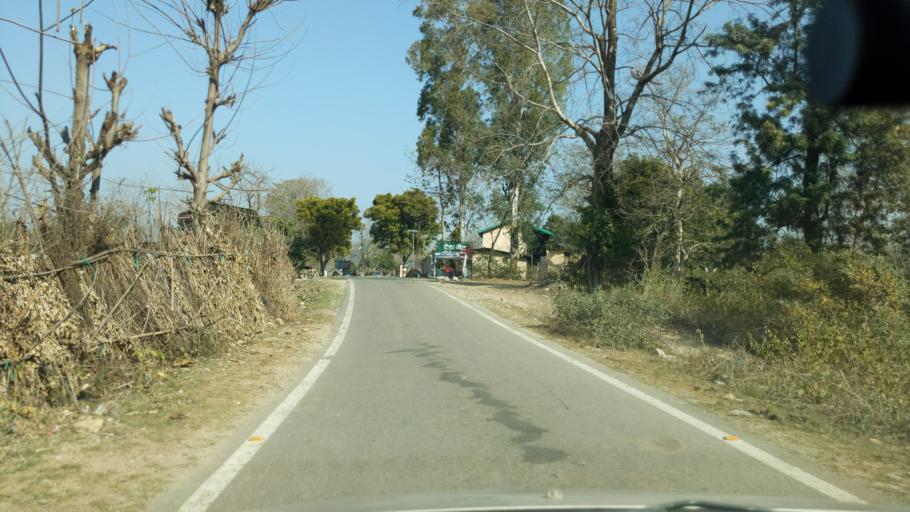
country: IN
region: Uttarakhand
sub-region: Naini Tal
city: Ramnagar
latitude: 29.4207
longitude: 79.1389
